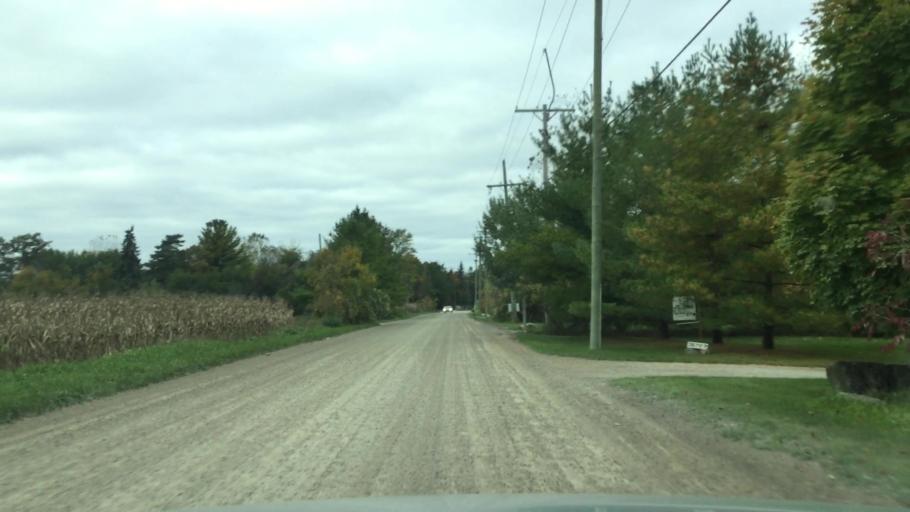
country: US
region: Michigan
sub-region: Macomb County
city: Richmond
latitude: 42.8224
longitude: -82.7471
